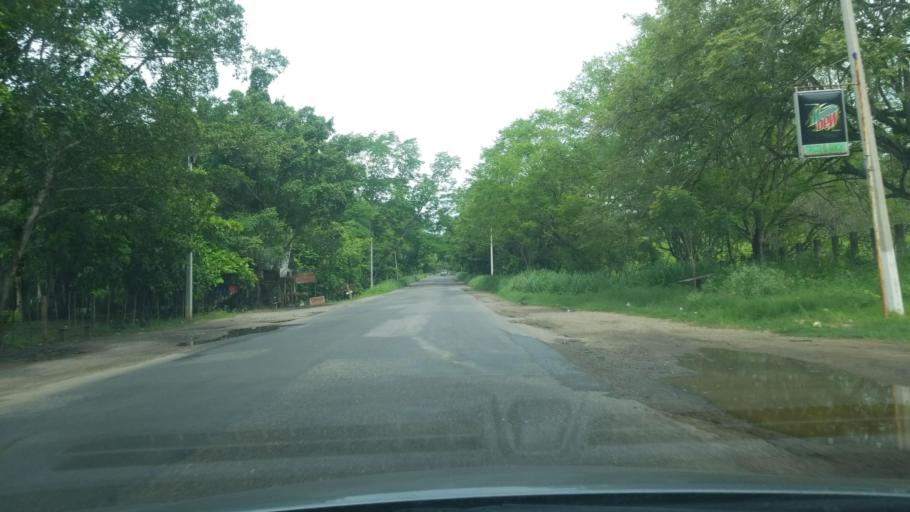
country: HN
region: Santa Barbara
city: Camalote
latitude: 15.3305
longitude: -88.3358
